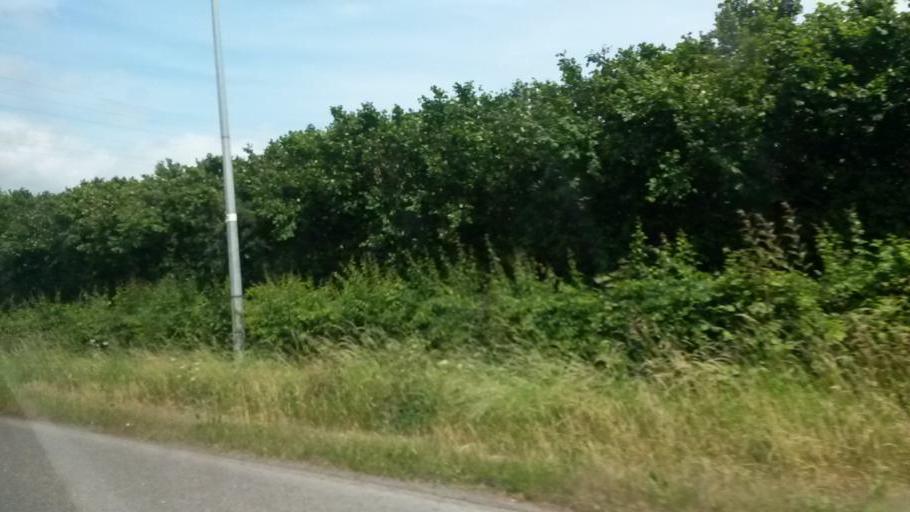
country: IE
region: Leinster
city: Balrothery
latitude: 53.5528
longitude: -6.2104
